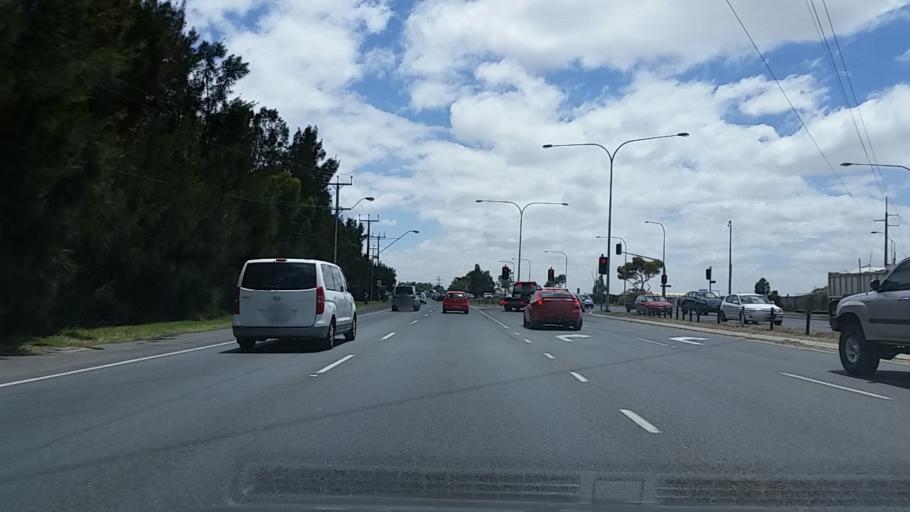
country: AU
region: South Australia
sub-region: Salisbury
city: Salisbury
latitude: -34.7949
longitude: 138.5965
